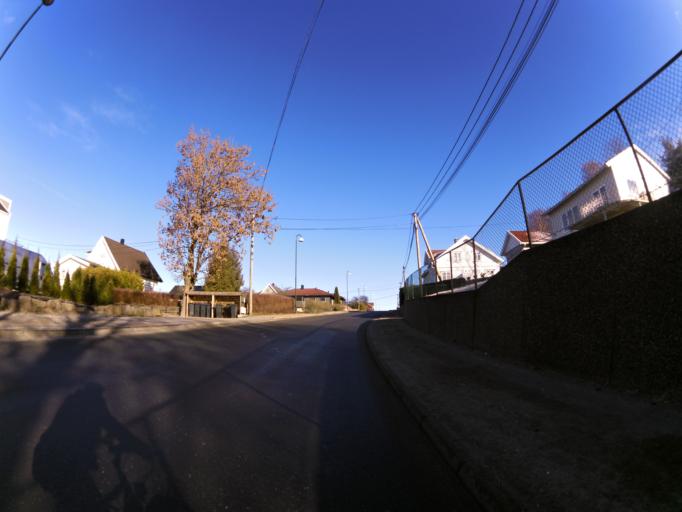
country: NO
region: Ostfold
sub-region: Sarpsborg
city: Sarpsborg
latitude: 59.2721
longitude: 11.0310
